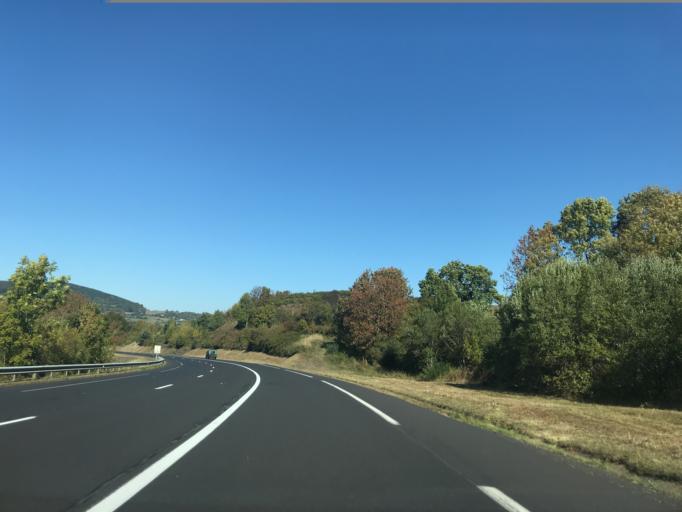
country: FR
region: Auvergne
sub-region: Departement du Puy-de-Dome
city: Gelles
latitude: 45.7174
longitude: 2.8063
